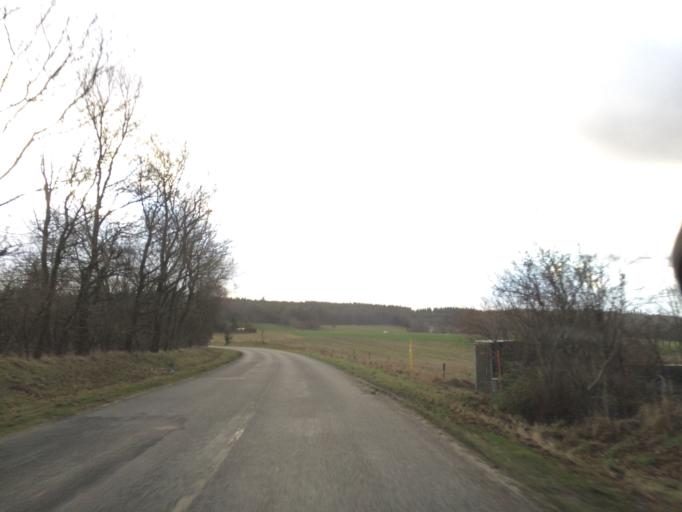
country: DK
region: Central Jutland
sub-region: Silkeborg Kommune
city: Svejbaek
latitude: 56.0954
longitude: 9.6723
